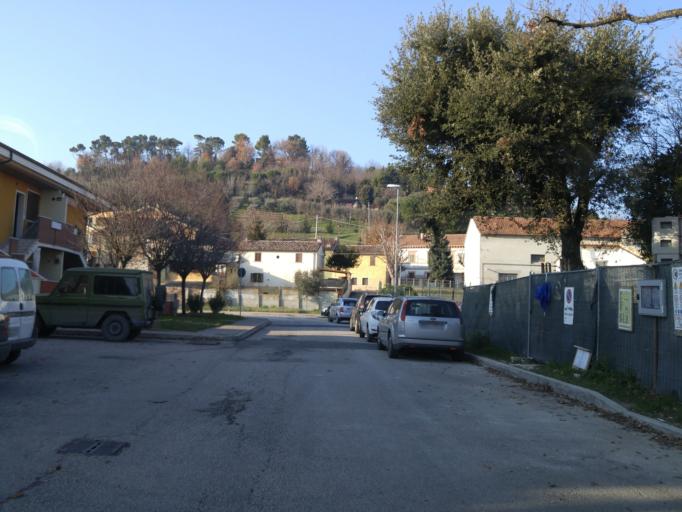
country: IT
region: The Marches
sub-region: Provincia di Pesaro e Urbino
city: Cuccurano
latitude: 43.8002
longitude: 12.9711
